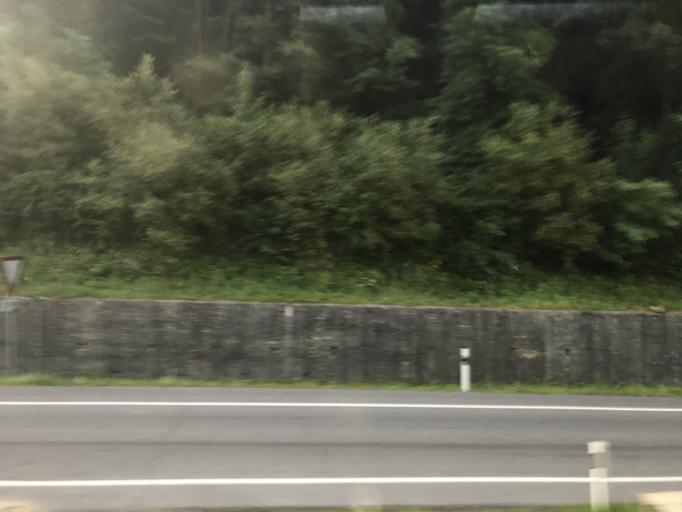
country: ES
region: Basque Country
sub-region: Provincia de Guipuzcoa
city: Icazteguieta
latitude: 43.0955
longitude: -2.1130
